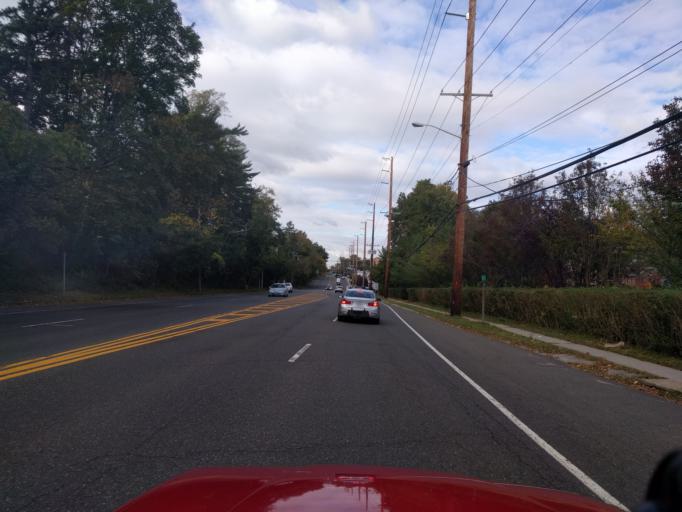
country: US
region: New York
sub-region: Nassau County
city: Munsey Park
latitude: 40.7949
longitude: -73.6824
